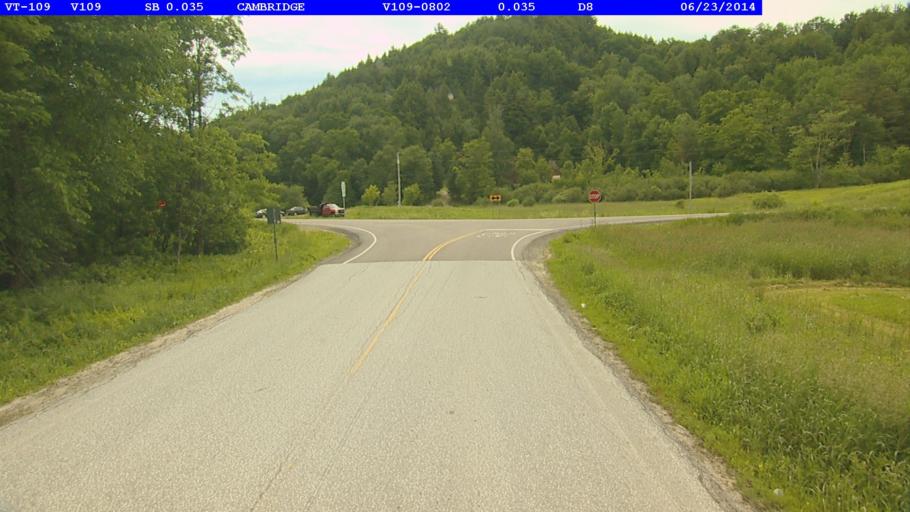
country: US
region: Vermont
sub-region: Lamoille County
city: Johnson
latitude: 44.6533
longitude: -72.8271
